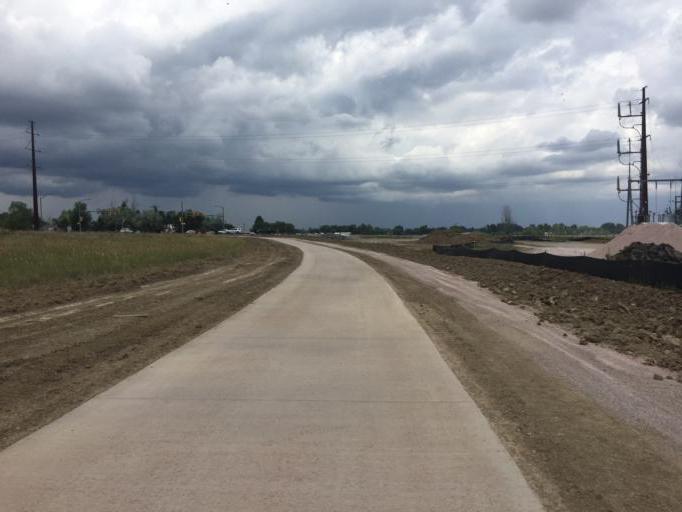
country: US
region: Colorado
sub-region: Larimer County
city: Fort Collins
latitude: 40.4930
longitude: -105.0954
